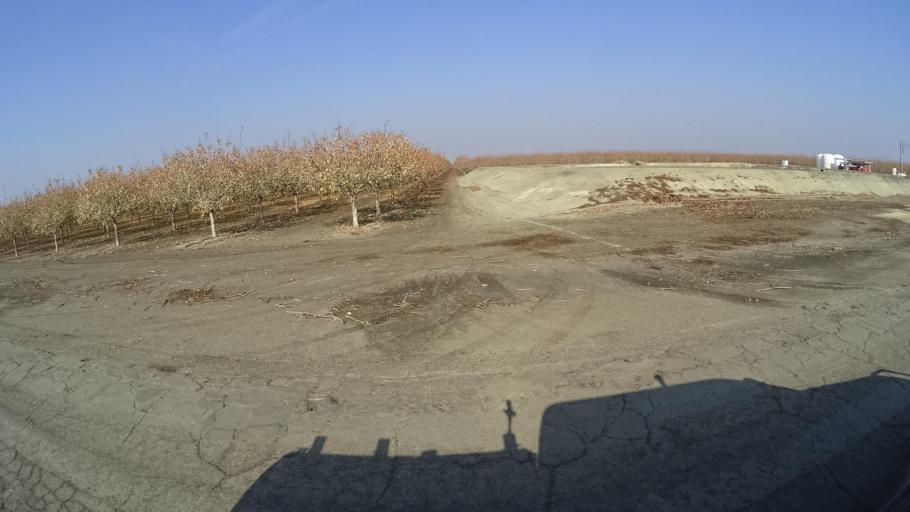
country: US
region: California
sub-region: Kern County
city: Buttonwillow
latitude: 35.3402
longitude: -119.4102
